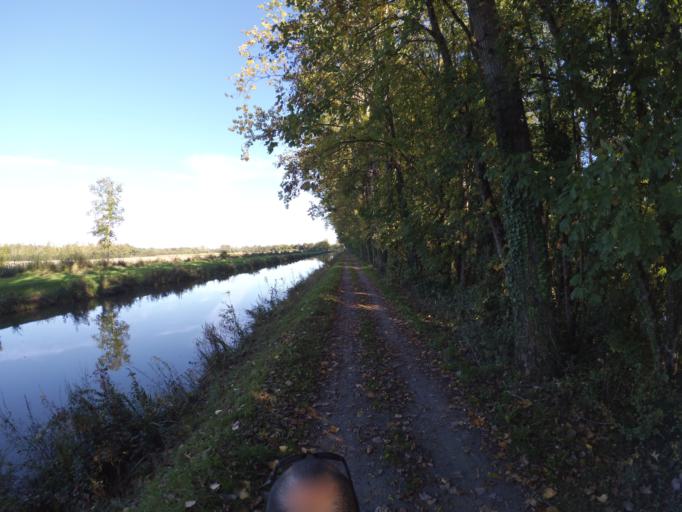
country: FR
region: Brittany
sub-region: Departement du Morbihan
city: Saint-Vincent-sur-Oust
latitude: 47.7193
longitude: -2.1614
